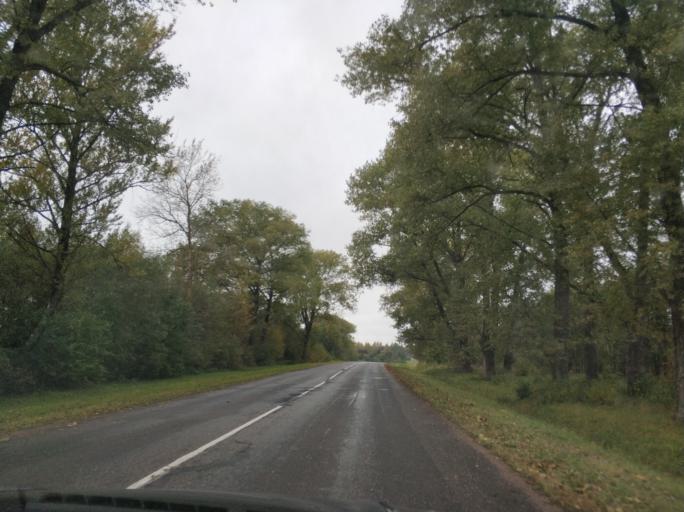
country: BY
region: Vitebsk
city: Polatsk
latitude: 55.4398
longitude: 28.9598
